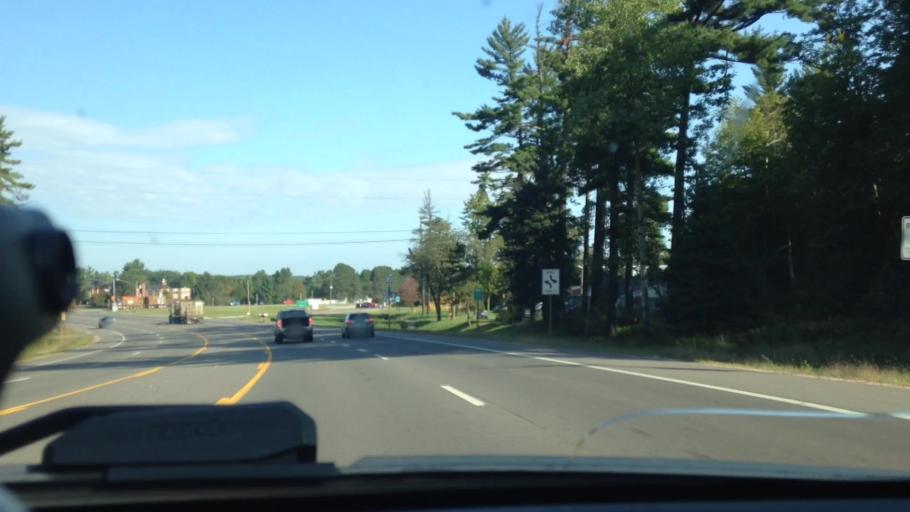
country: US
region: Michigan
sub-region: Dickinson County
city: Iron Mountain
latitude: 45.8609
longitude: -88.0602
